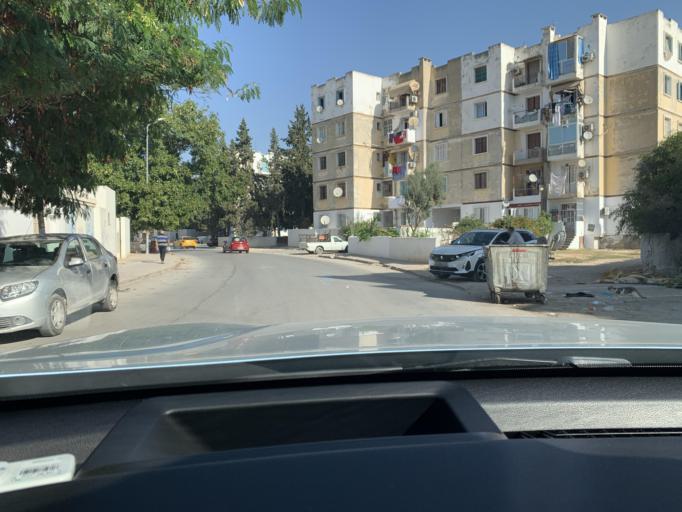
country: TN
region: Manouba
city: Manouba
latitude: 36.8235
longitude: 10.1191
